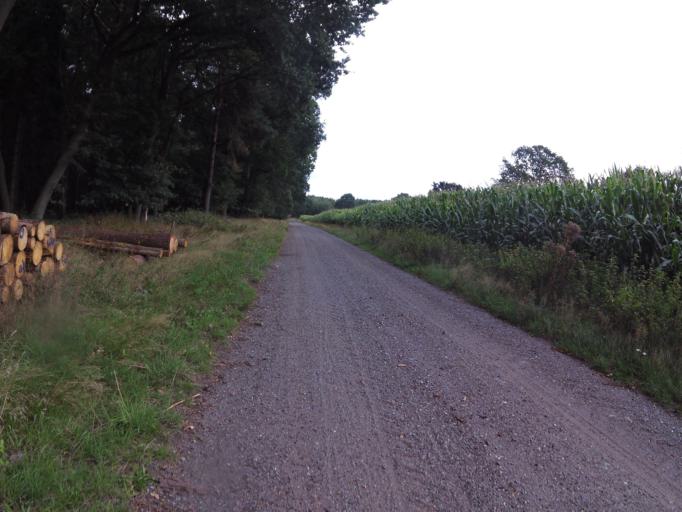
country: DE
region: Lower Saxony
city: Hipstedt
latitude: 53.5006
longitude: 8.9309
